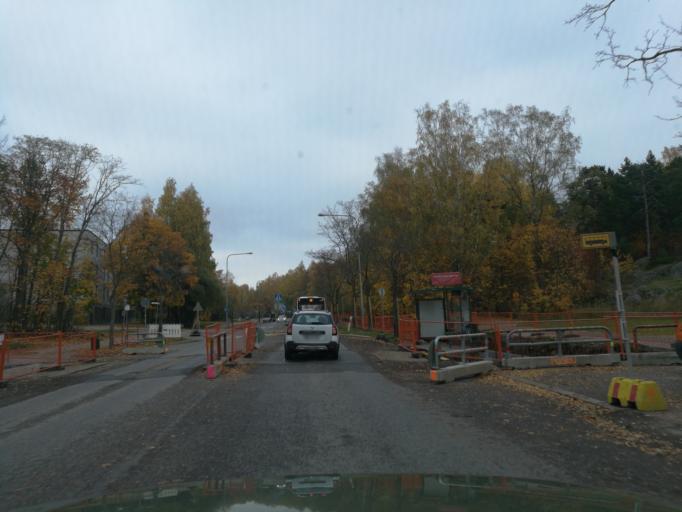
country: FI
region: Uusimaa
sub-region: Helsinki
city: Helsinki
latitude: 60.2235
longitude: 24.9658
